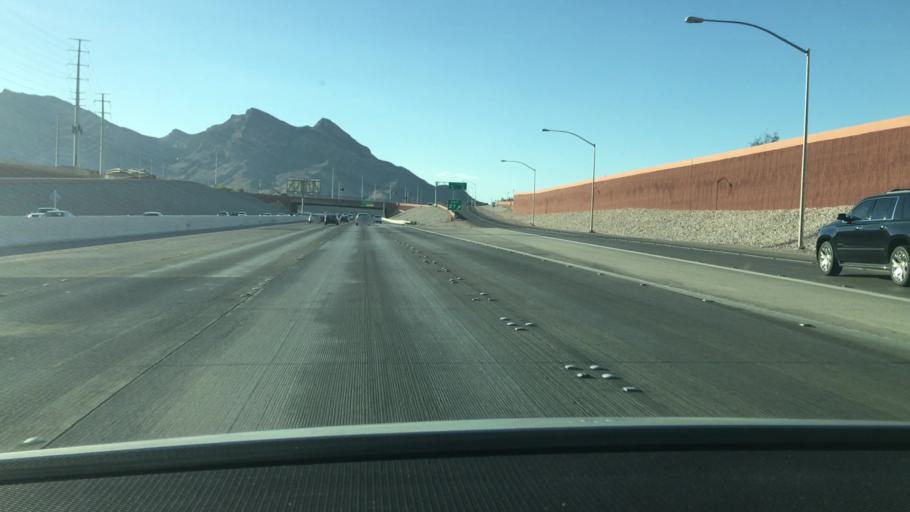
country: US
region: Nevada
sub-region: Clark County
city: Summerlin South
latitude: 36.1772
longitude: -115.3391
